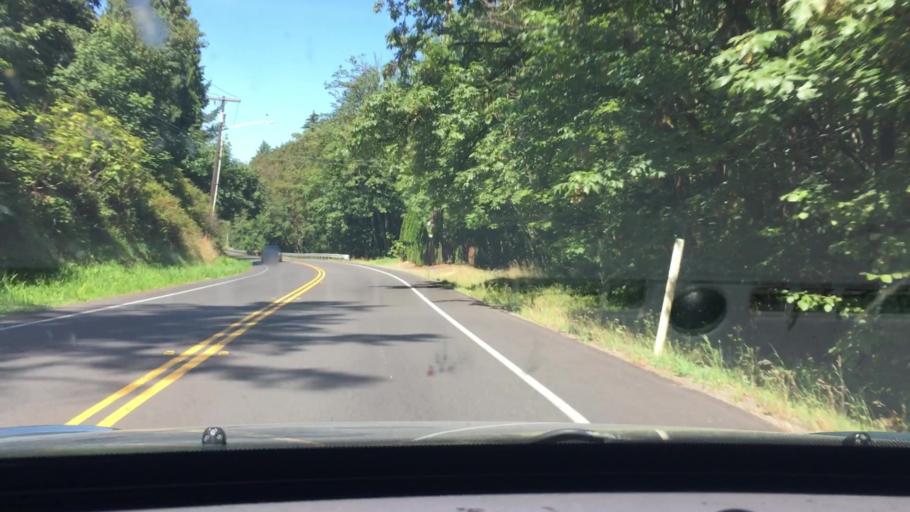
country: US
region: Washington
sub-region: King County
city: Newcastle
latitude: 47.5394
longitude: -122.1429
